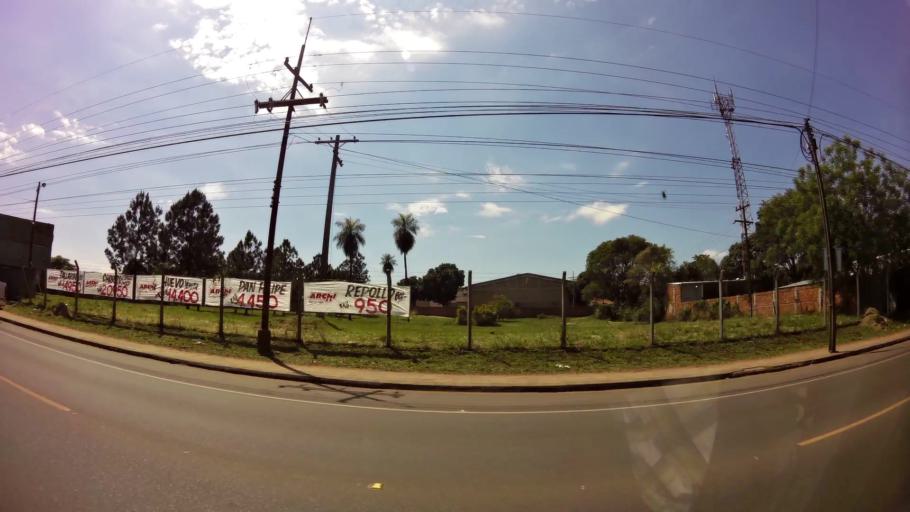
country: PY
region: Central
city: San Lorenzo
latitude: -25.2978
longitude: -57.5030
